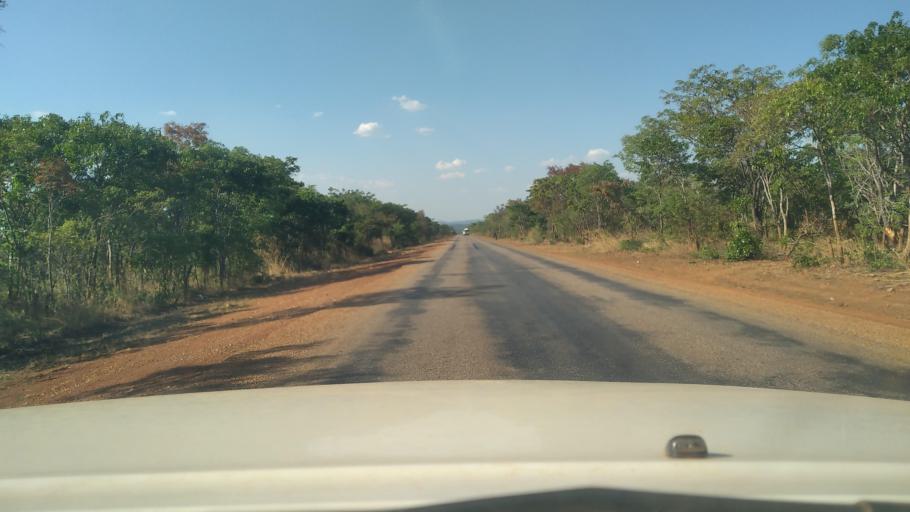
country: ZM
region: Northern
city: Mpika
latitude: -11.7691
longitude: 31.4623
